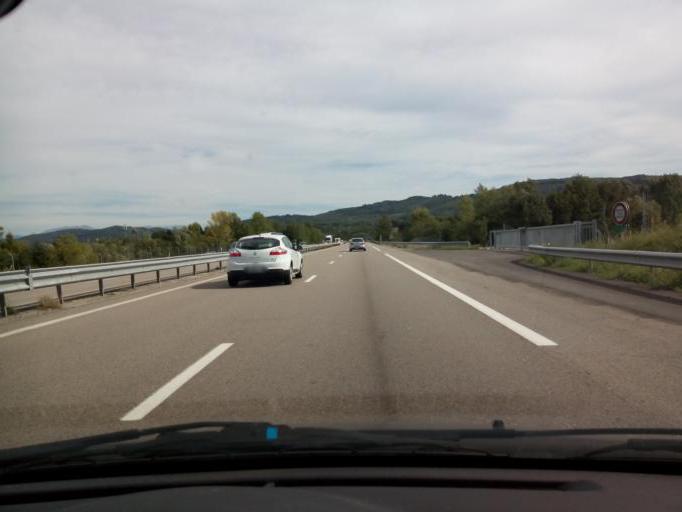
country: FR
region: Rhone-Alpes
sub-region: Departement de l'Isere
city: Chabons
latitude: 45.4338
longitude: 5.4219
